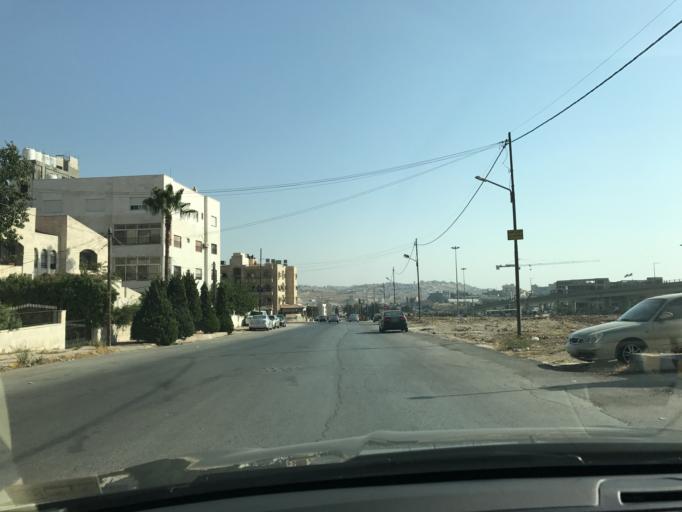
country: JO
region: Amman
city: Wadi as Sir
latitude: 31.9471
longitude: 35.8515
